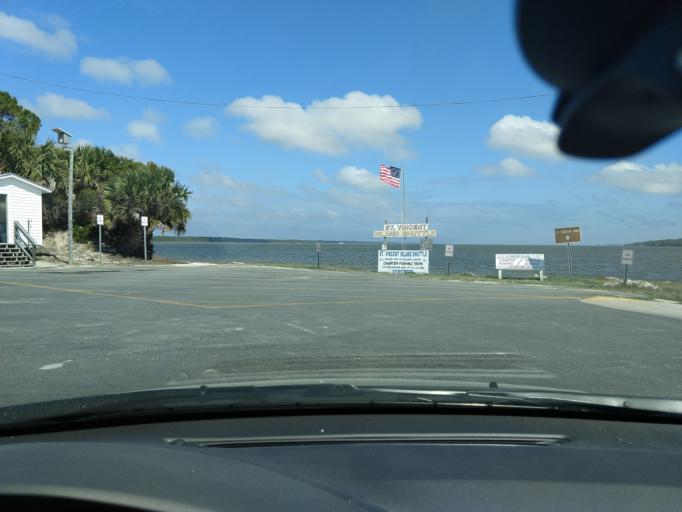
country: US
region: Florida
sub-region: Gulf County
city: Port Saint Joe
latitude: 29.6834
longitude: -85.2229
